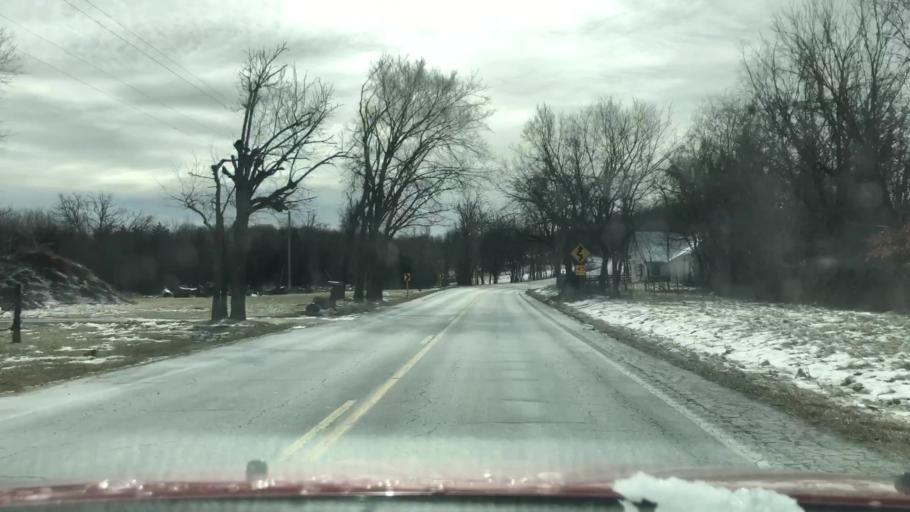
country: US
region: Missouri
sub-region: Jackson County
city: Oak Grove
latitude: 38.9423
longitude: -94.1321
